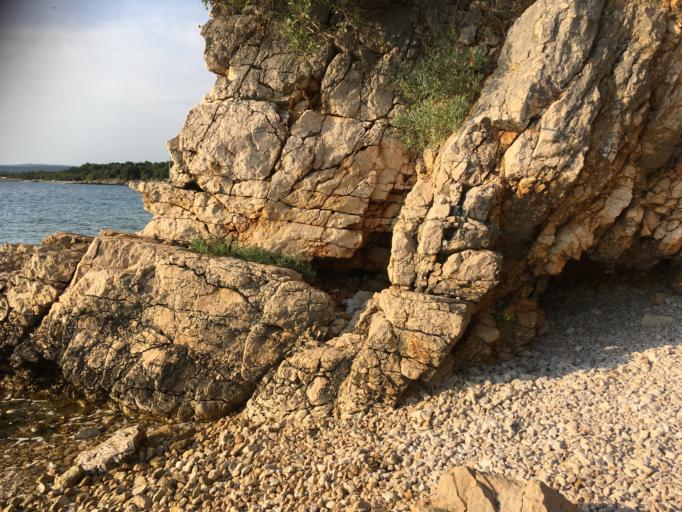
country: HR
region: Primorsko-Goranska
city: Punat
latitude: 44.9977
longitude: 14.6263
